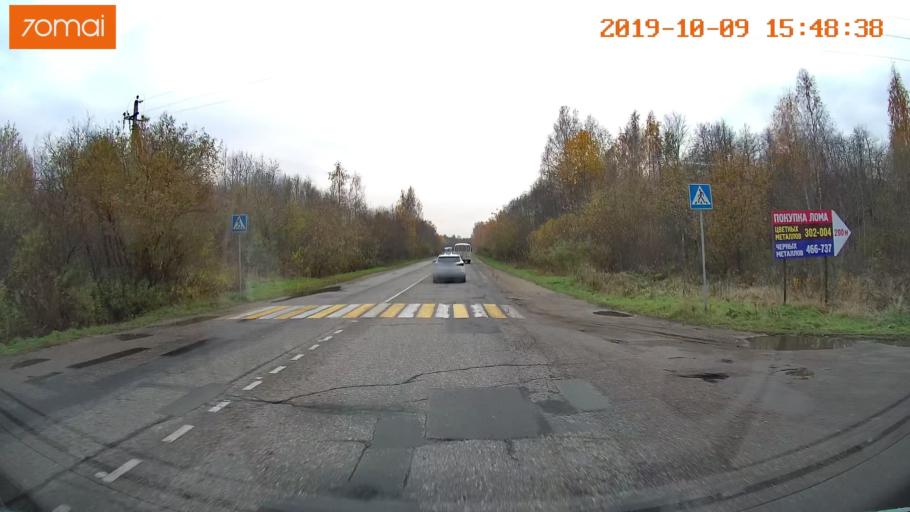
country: RU
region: Kostroma
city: Oktyabr'skiy
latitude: 57.8107
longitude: 41.0128
